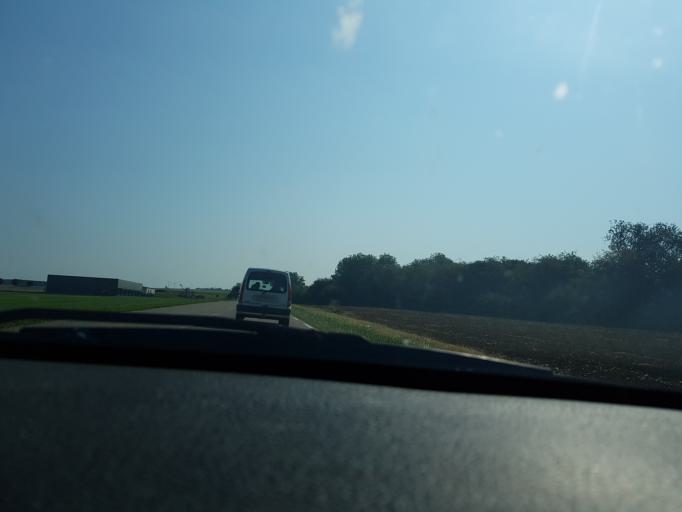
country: FR
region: Lorraine
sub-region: Departement de la Moselle
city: Verny
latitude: 48.9638
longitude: 6.2156
